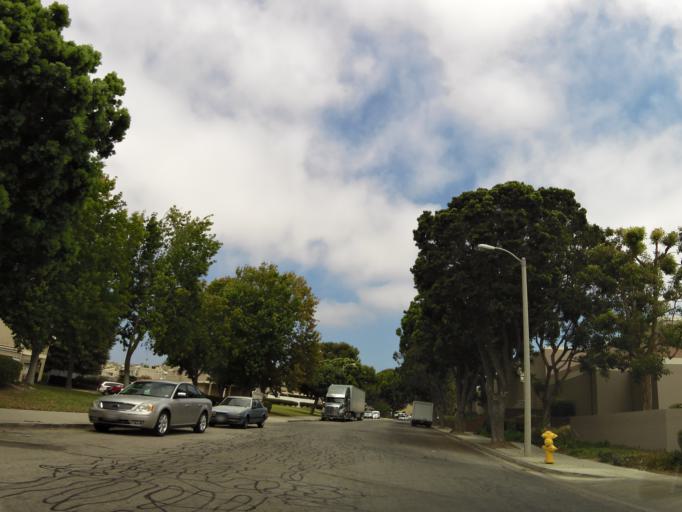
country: US
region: California
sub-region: Ventura County
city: El Rio
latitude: 34.2615
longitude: -119.2140
